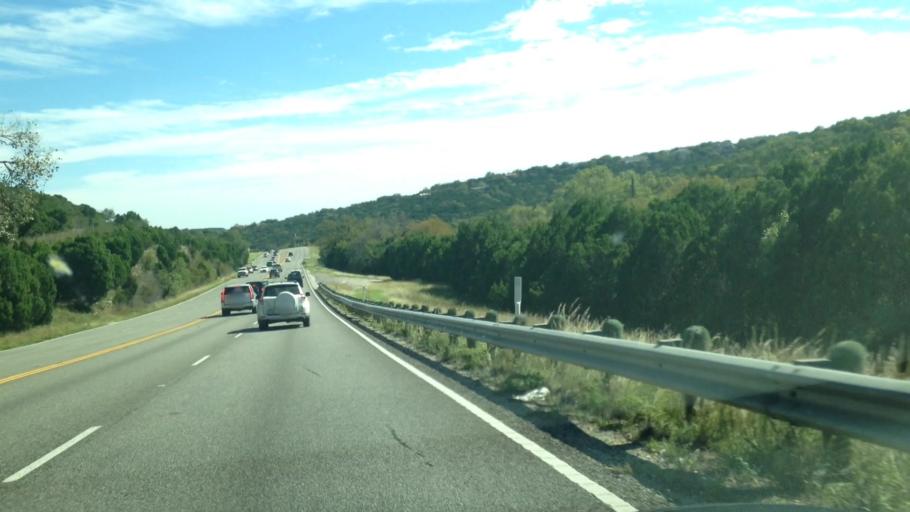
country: US
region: Texas
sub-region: Williamson County
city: Anderson Mill
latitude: 30.3867
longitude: -97.8230
